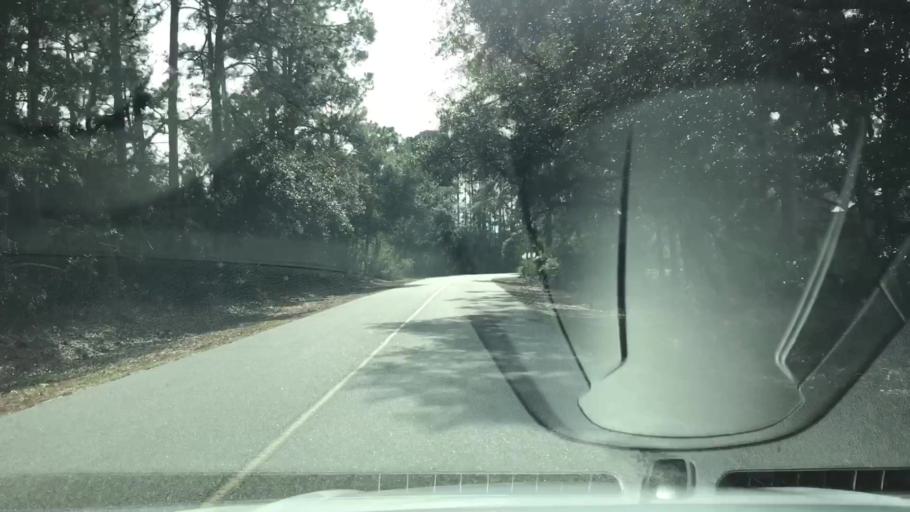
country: US
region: South Carolina
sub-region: Beaufort County
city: Hilton Head Island
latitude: 32.2413
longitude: -80.7082
